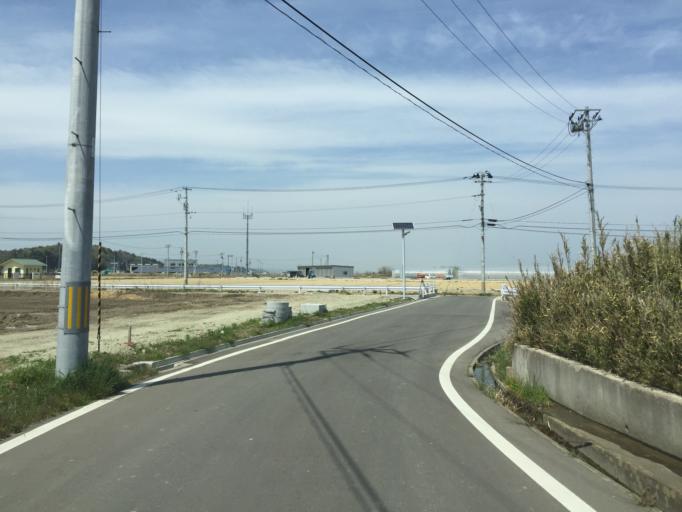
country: JP
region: Miyagi
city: Watari
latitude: 37.8994
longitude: 140.9255
